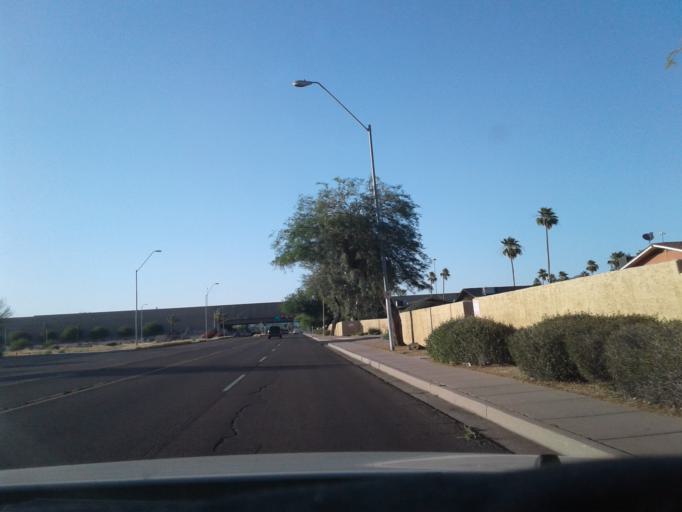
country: US
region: Arizona
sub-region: Maricopa County
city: Tempe Junction
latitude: 33.4563
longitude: -111.9952
